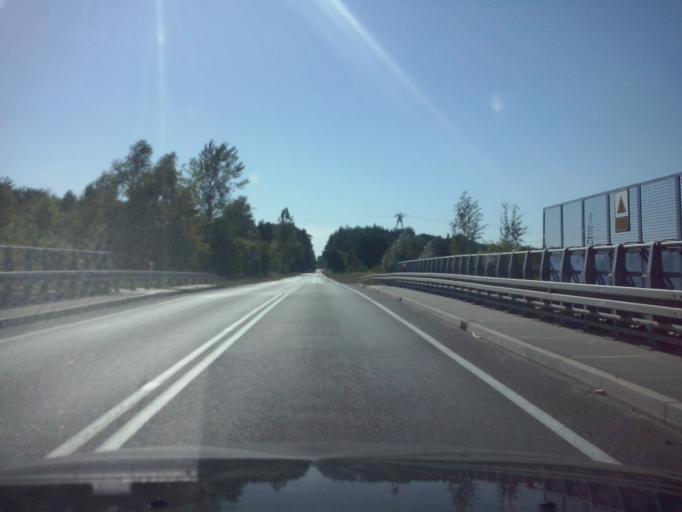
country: PL
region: Swietokrzyskie
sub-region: Powiat kielecki
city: Chmielnik
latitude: 50.6090
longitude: 20.7088
